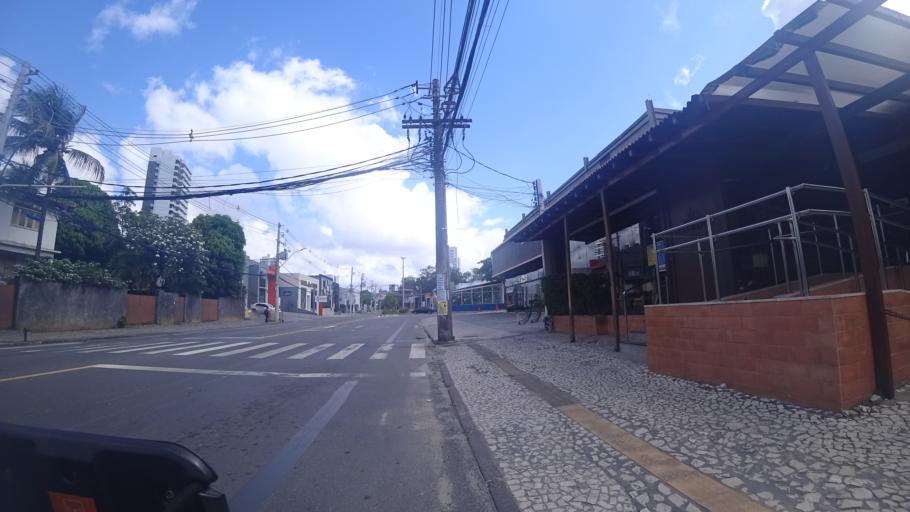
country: BR
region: Bahia
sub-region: Salvador
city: Salvador
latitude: -12.9863
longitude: -38.4574
